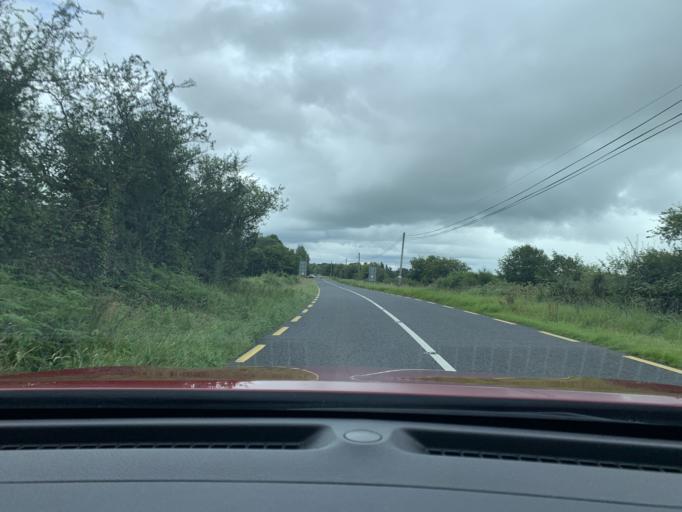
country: IE
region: Ulster
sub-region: County Donegal
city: Convoy
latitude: 54.8007
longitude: -7.6354
